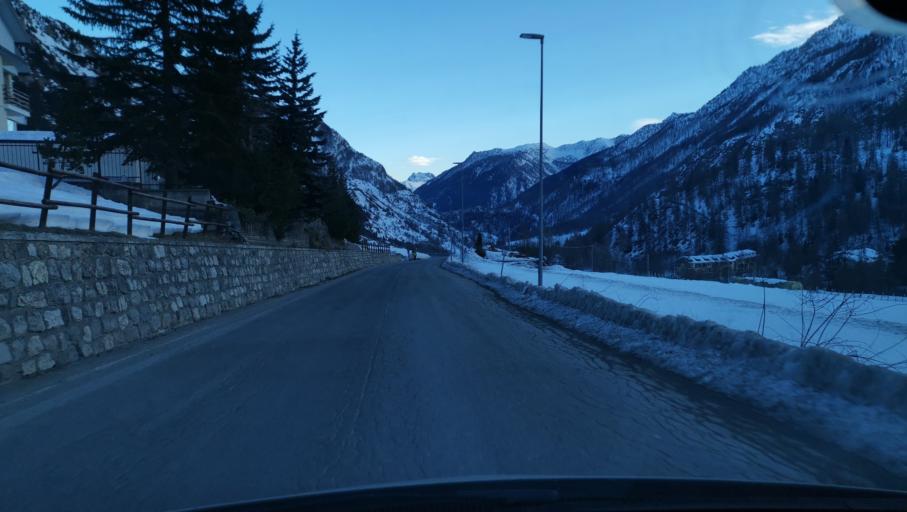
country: IT
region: Piedmont
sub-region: Provincia di Cuneo
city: Bersezio
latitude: 44.3754
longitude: 6.9736
